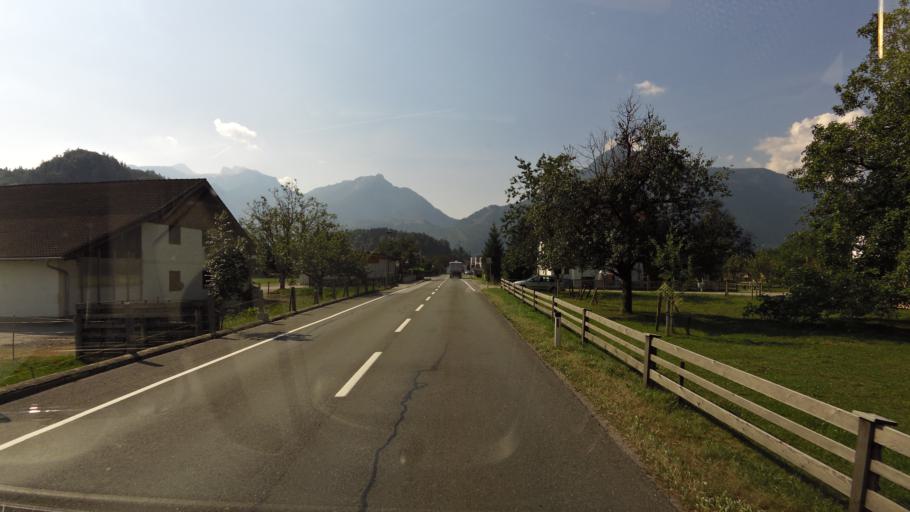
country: AT
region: Salzburg
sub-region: Politischer Bezirk Hallein
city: Golling an der Salzach
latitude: 47.6057
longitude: 13.1679
